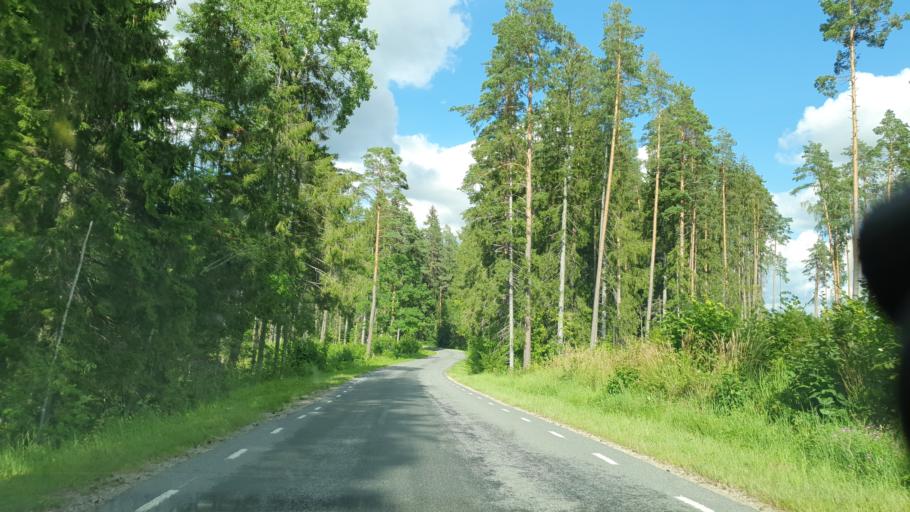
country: EE
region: Jogevamaa
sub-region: Tabivere vald
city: Tabivere
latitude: 58.6335
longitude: 26.6029
